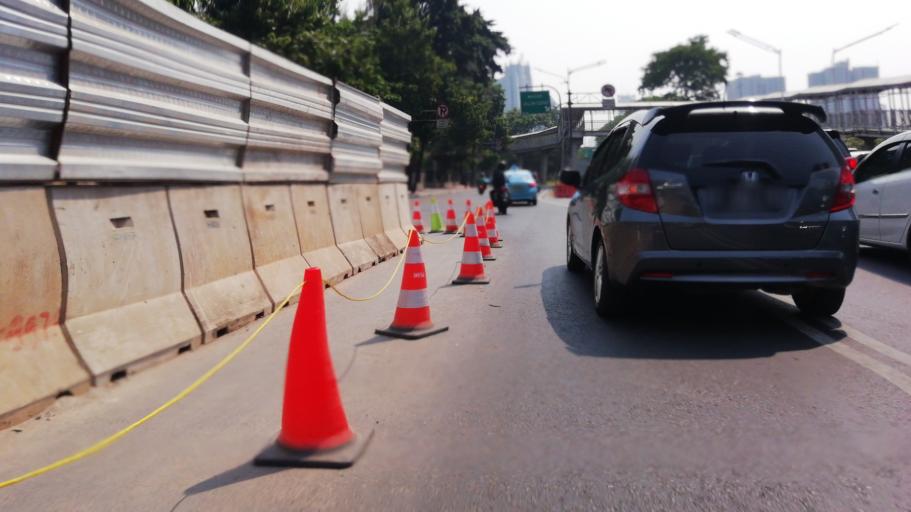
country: ID
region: Jakarta Raya
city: Jakarta
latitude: -6.2174
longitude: 106.8153
